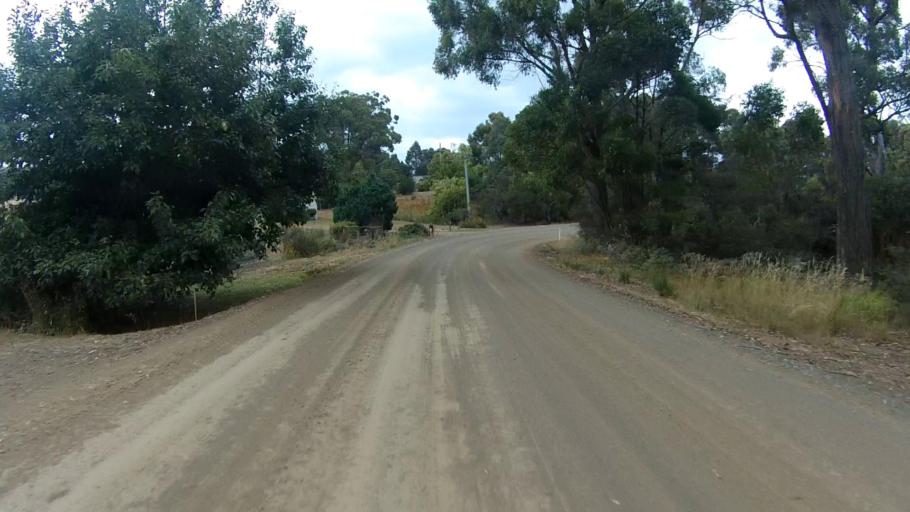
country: AU
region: Tasmania
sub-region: Huon Valley
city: Cygnet
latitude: -43.2252
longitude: 147.0975
